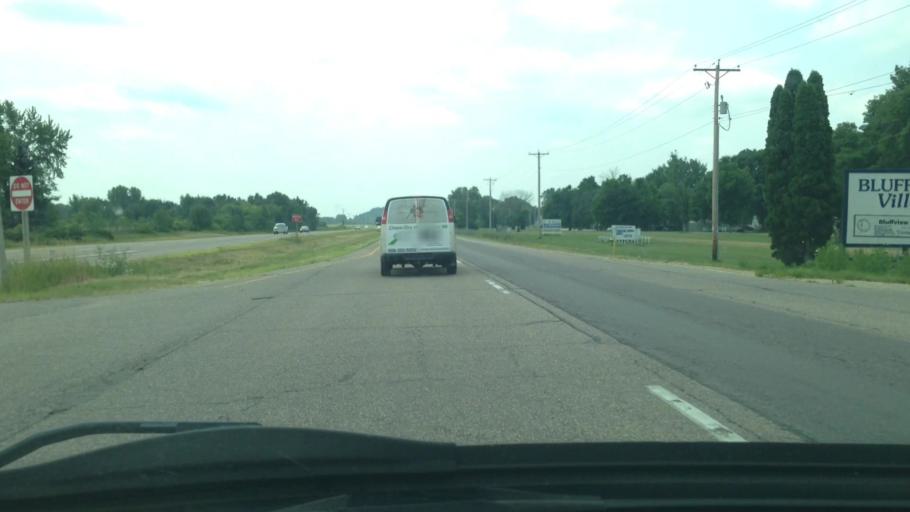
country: US
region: Wisconsin
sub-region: Sauk County
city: Prairie du Sac
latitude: 43.3701
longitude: -89.7687
